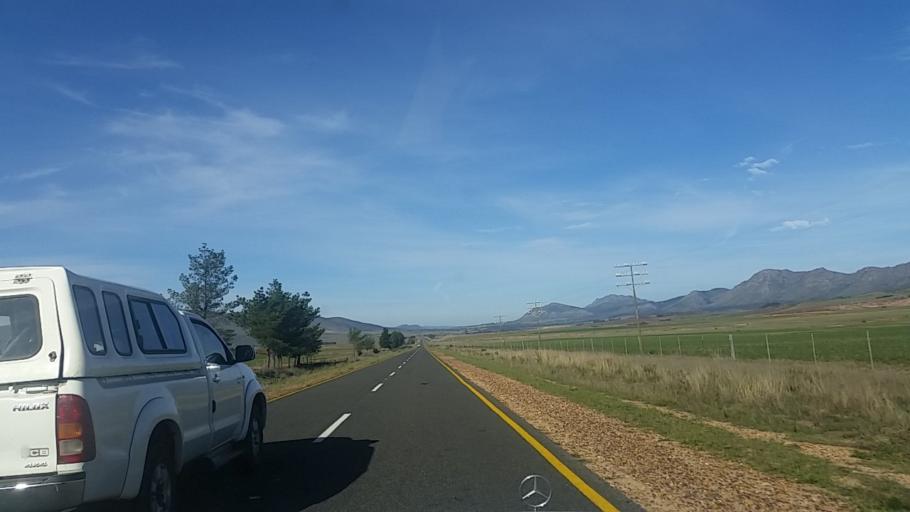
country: ZA
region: Western Cape
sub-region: Eden District Municipality
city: George
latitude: -33.8162
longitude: 22.5142
